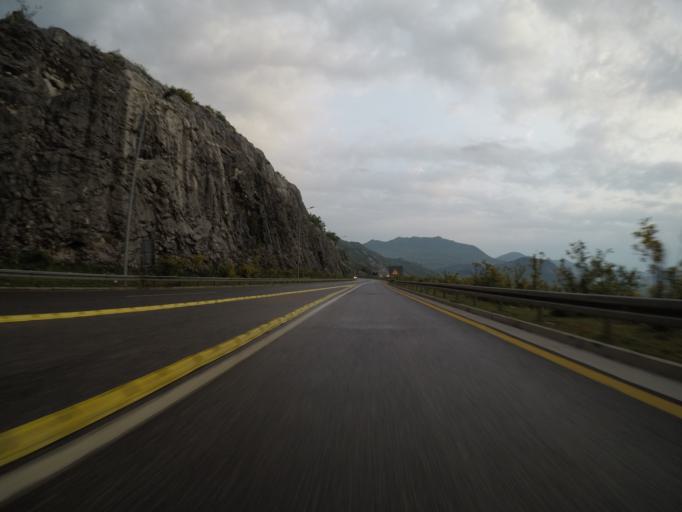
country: ME
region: Bar
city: Sutomore
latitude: 42.2050
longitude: 19.0504
